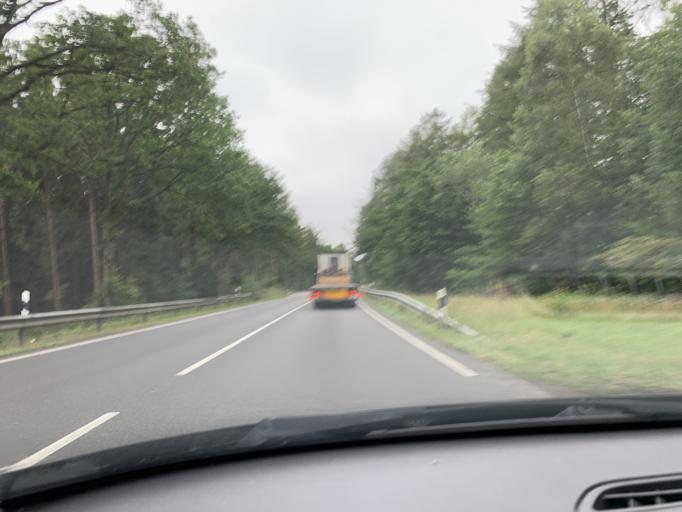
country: DE
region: Lower Saxony
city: Haselunne
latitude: 52.6443
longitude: 7.4694
